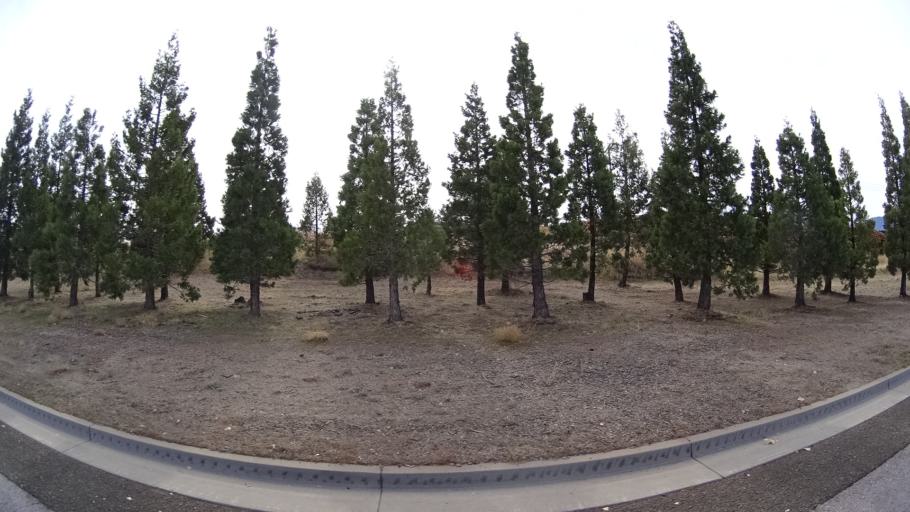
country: US
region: California
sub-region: Siskiyou County
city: Weed
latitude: 41.4360
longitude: -122.3804
